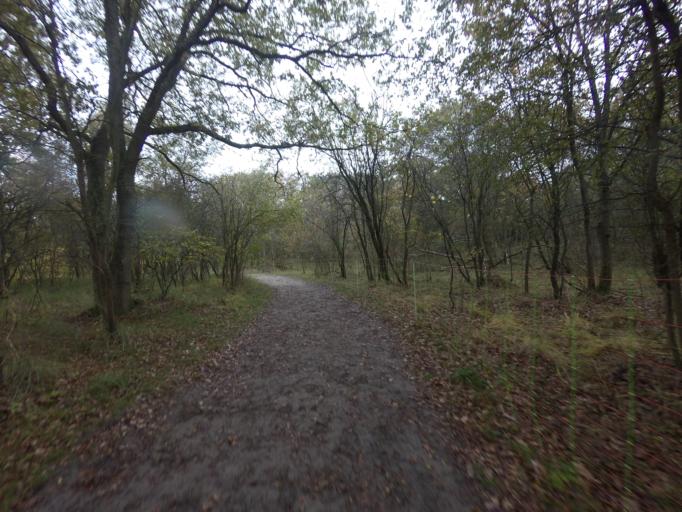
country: NL
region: South Holland
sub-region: Gemeente Wassenaar
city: Wassenaar
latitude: 52.1330
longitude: 4.3454
